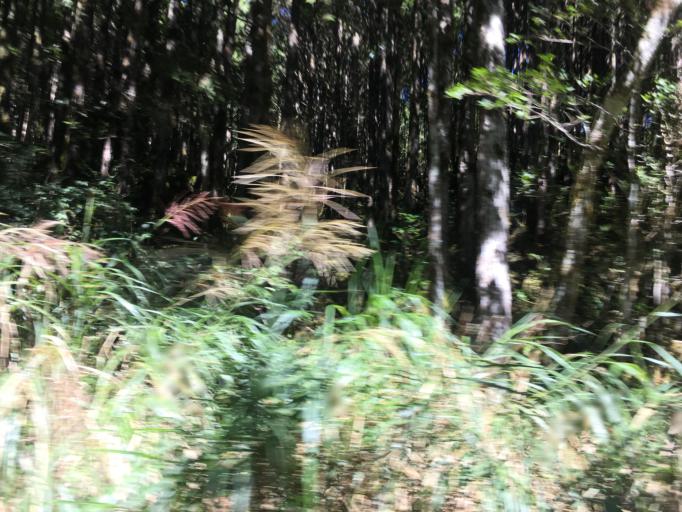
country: TW
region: Taiwan
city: Daxi
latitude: 24.5918
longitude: 121.4202
